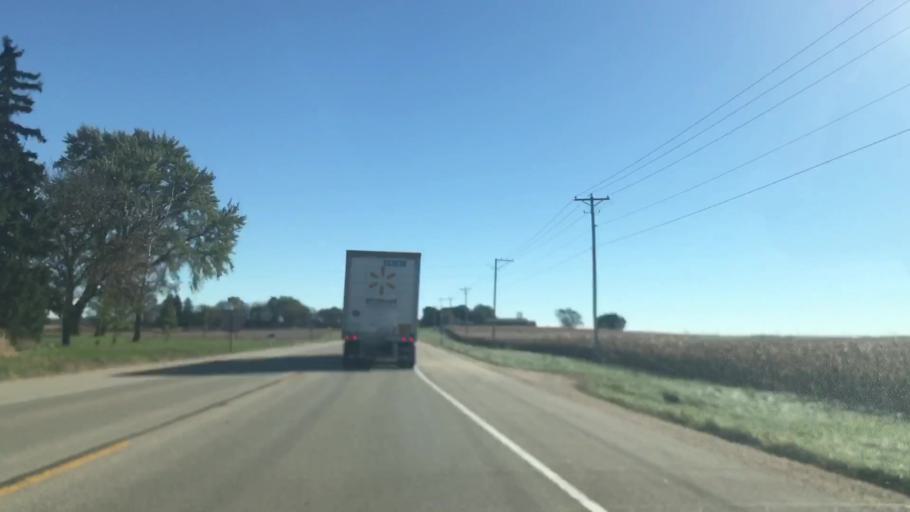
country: US
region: Wisconsin
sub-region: Dodge County
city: Juneau
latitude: 43.4446
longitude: -88.7489
